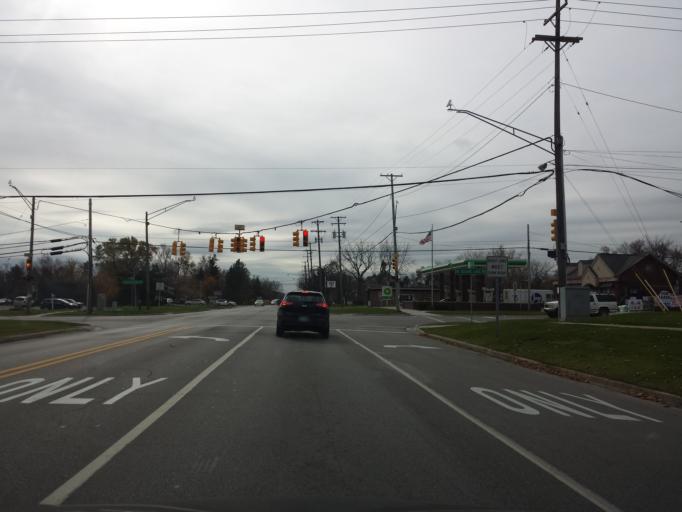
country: US
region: Michigan
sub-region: Oakland County
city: Troy
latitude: 42.6069
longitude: -83.1498
